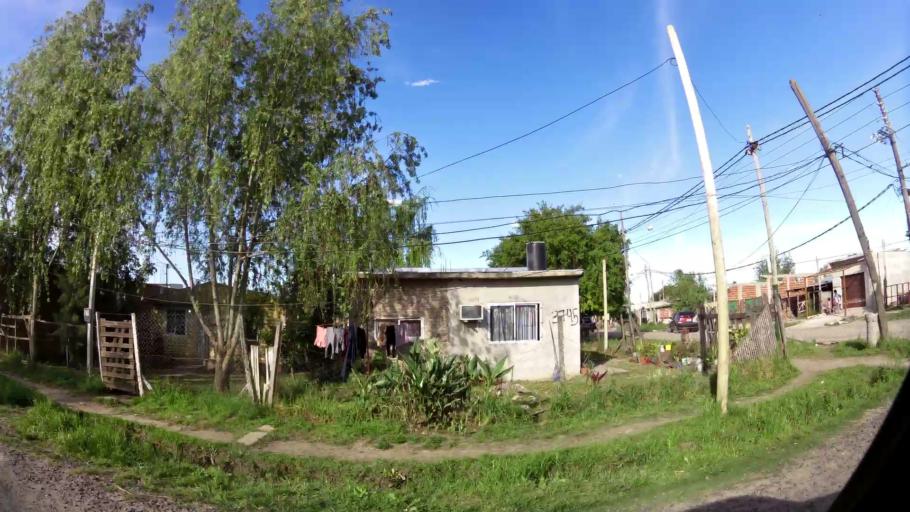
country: AR
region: Buenos Aires
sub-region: Partido de Almirante Brown
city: Adrogue
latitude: -34.8149
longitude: -58.3293
